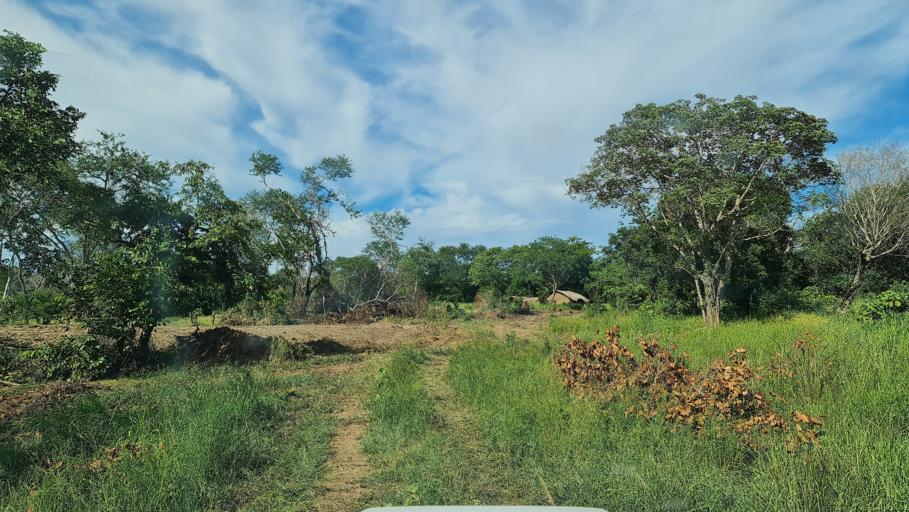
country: MZ
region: Nampula
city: Ilha de Mocambique
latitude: -15.5081
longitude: 40.1426
